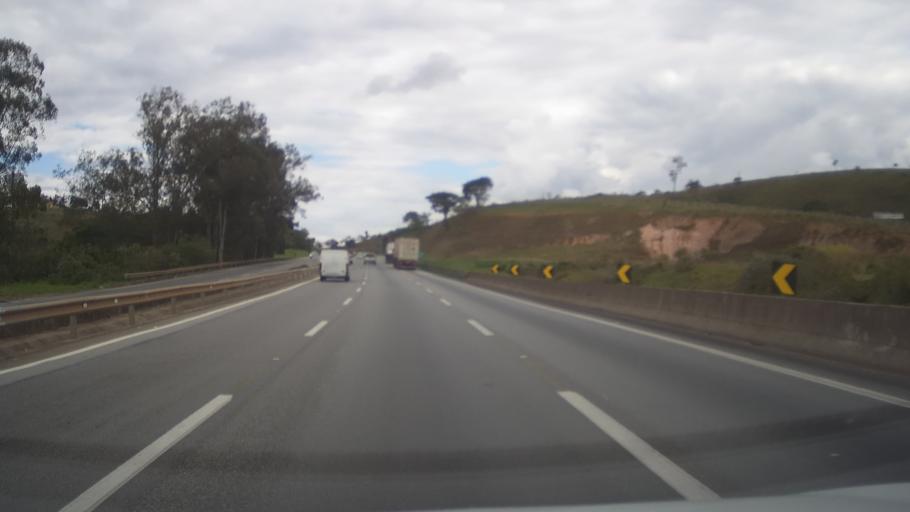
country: BR
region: Minas Gerais
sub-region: Itauna
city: Itauna
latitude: -20.3495
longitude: -44.4445
